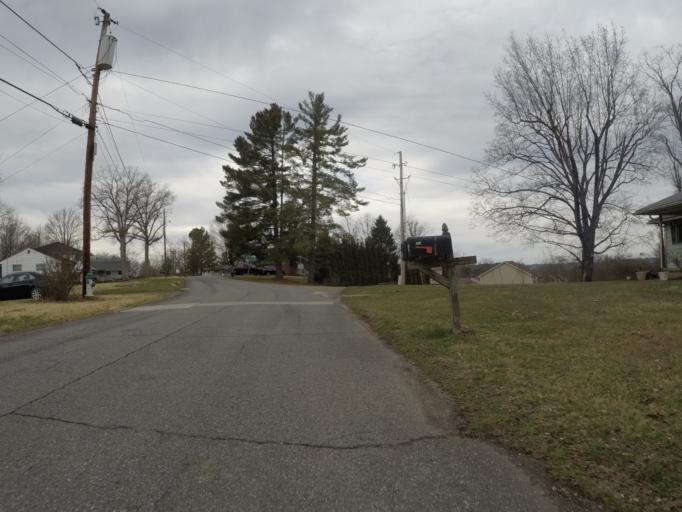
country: US
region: West Virginia
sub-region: Cabell County
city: Huntington
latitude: 38.3965
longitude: -82.3836
